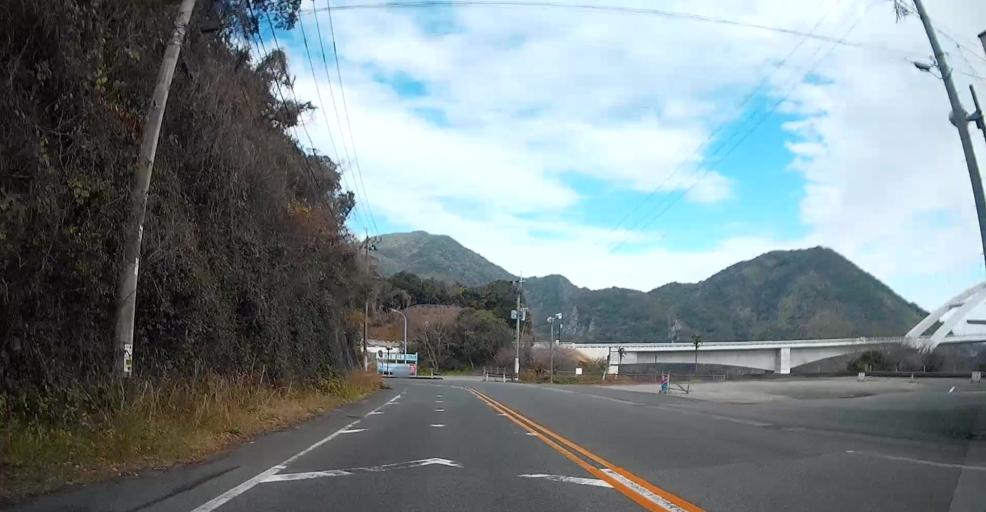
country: JP
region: Kumamoto
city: Yatsushiro
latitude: 32.6126
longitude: 130.4563
